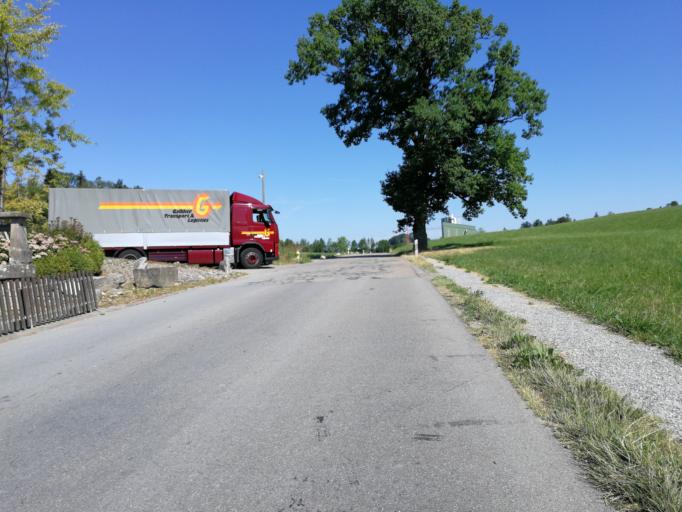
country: CH
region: Zurich
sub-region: Bezirk Hinwil
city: Gossau
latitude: 47.3108
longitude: 8.7534
